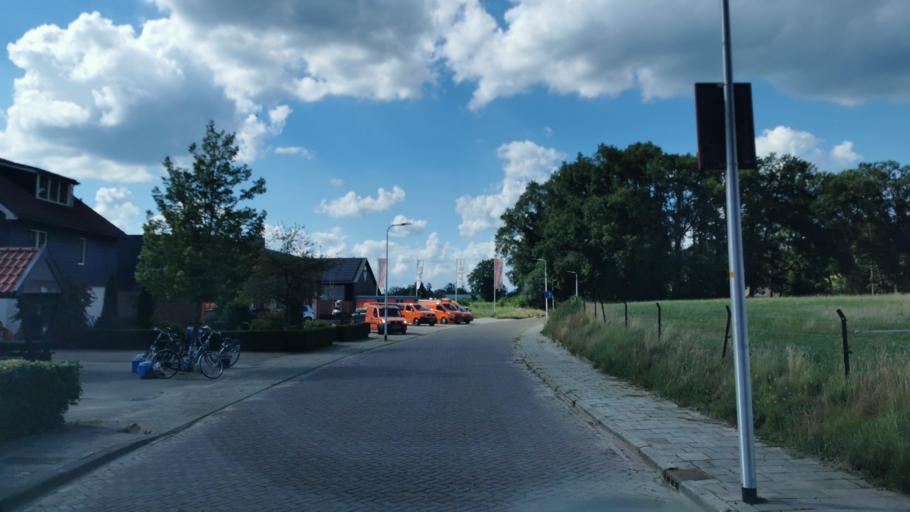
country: DE
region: Lower Saxony
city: Lage
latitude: 52.4284
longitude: 6.9764
